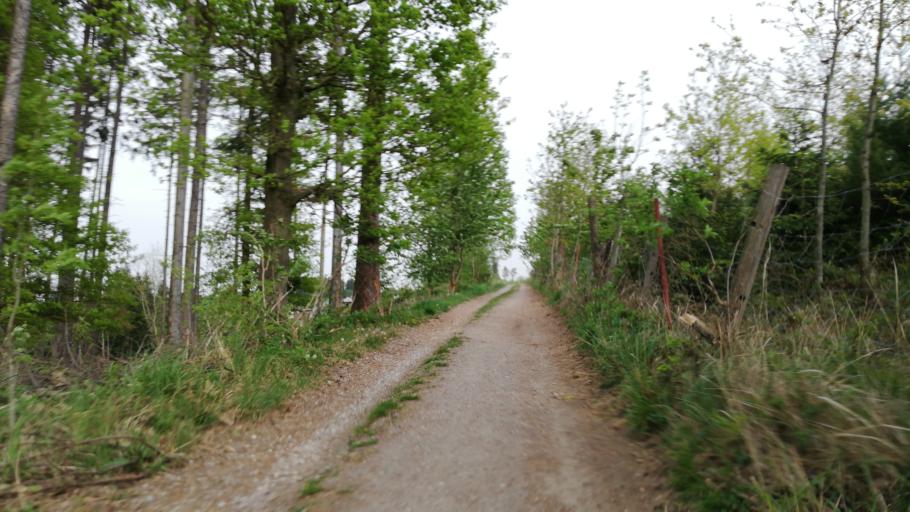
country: AT
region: Upper Austria
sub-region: Wels-Land
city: Gunskirchen
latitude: 48.1823
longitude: 13.9519
